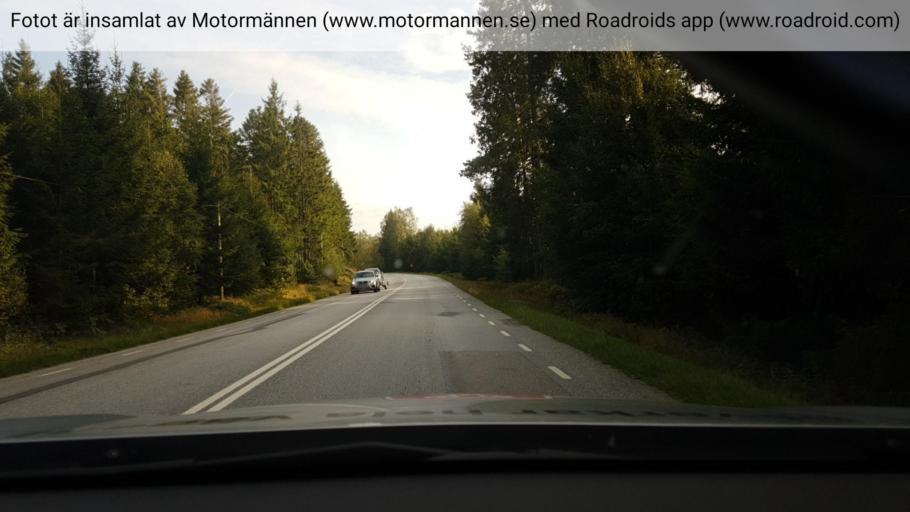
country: SE
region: Vaestra Goetaland
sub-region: Uddevalla Kommun
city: Ljungskile
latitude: 58.1728
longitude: 11.9635
